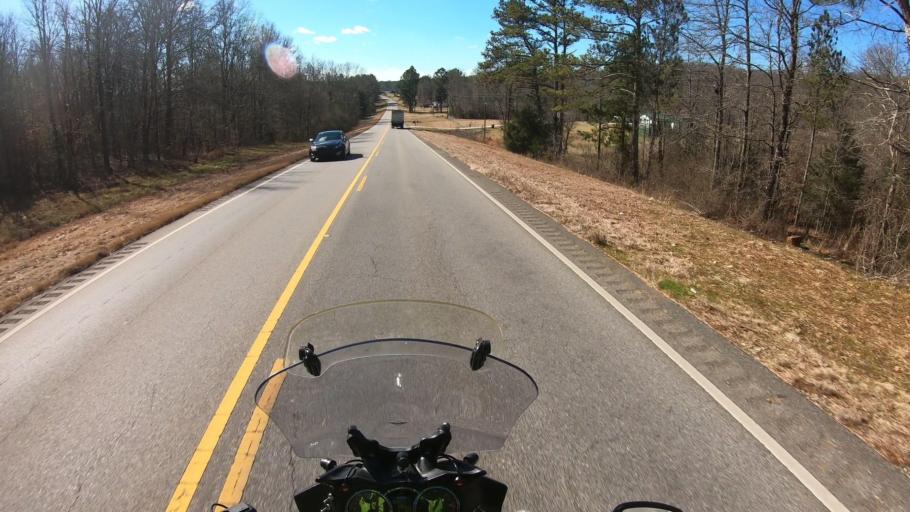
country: US
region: Alabama
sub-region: Cleburne County
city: Heflin
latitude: 33.5114
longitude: -85.6494
